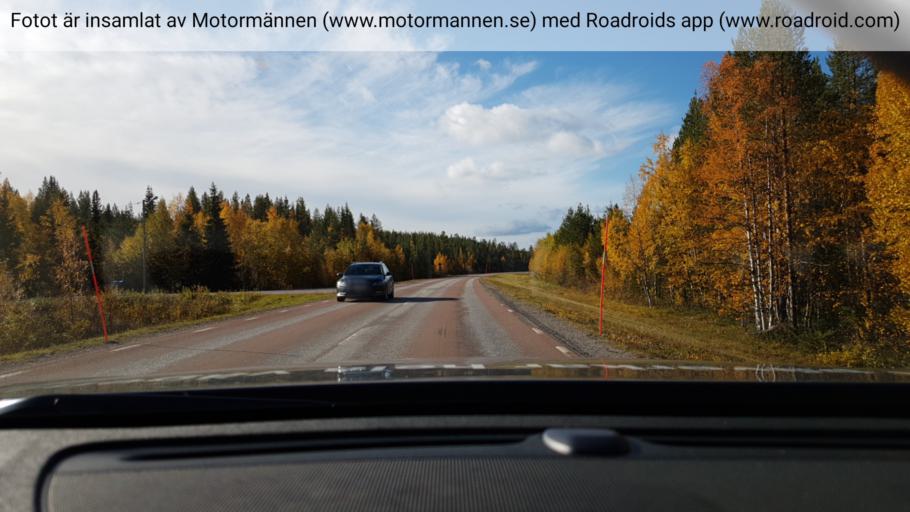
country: SE
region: Norrbotten
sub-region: Arjeplogs Kommun
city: Arjeplog
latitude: 66.0554
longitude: 17.9284
